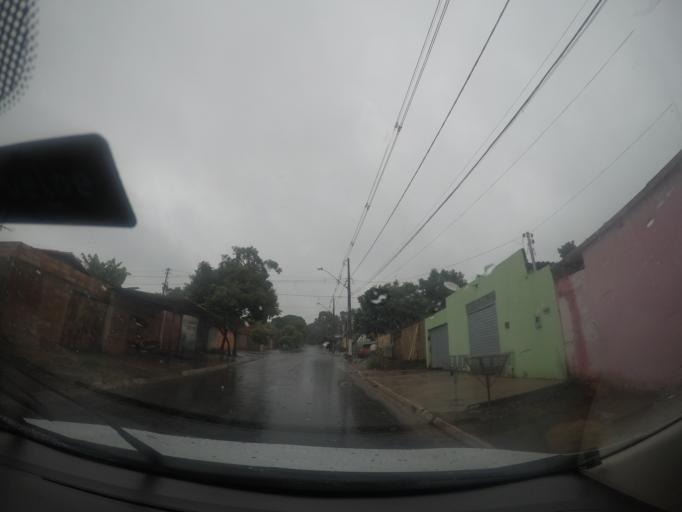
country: BR
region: Goias
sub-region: Goianira
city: Goianira
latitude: -16.5871
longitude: -49.3416
